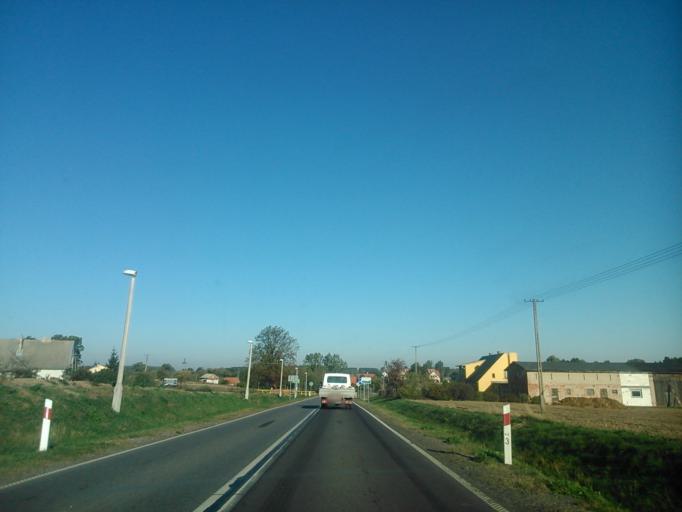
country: PL
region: Kujawsko-Pomorskie
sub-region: Powiat wabrzeski
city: Debowa Laka
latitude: 53.1976
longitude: 19.0379
